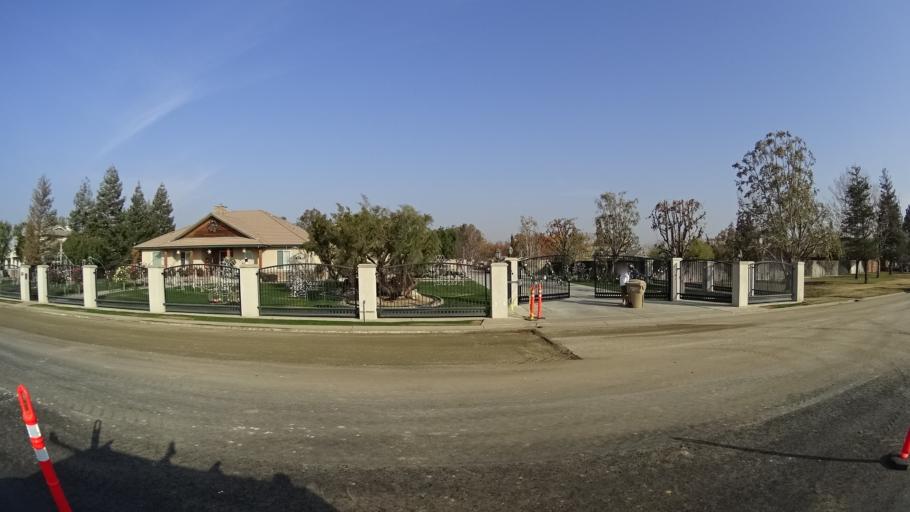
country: US
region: California
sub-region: Kern County
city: Greenacres
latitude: 35.4341
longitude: -119.1037
